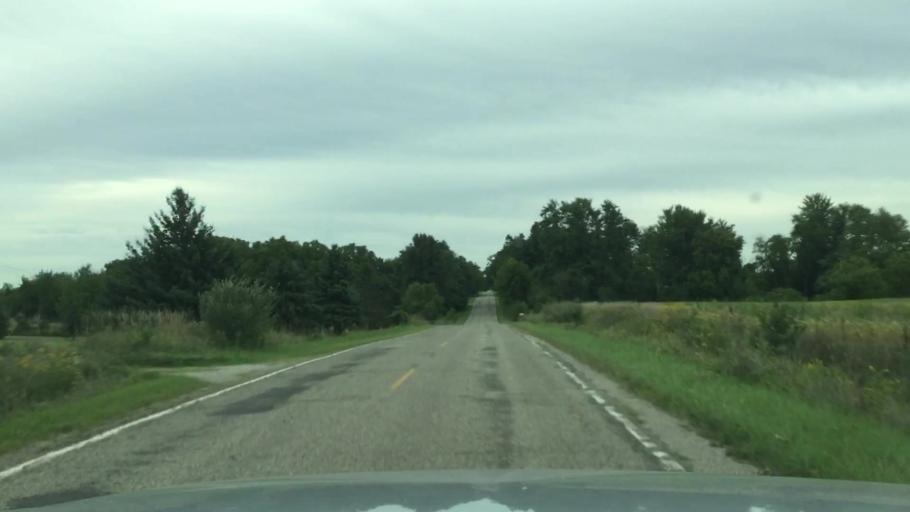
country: US
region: Michigan
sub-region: Shiawassee County
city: Durand
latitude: 42.8996
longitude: -84.0692
